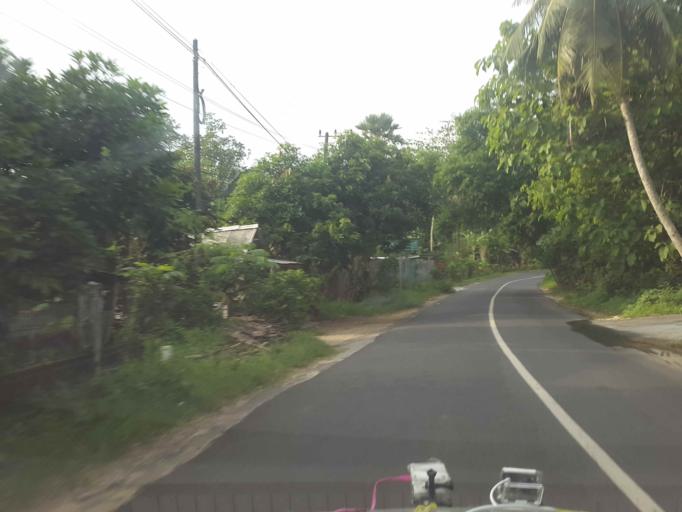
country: ID
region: East Java
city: Senmasen
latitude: -6.9896
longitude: 113.8632
